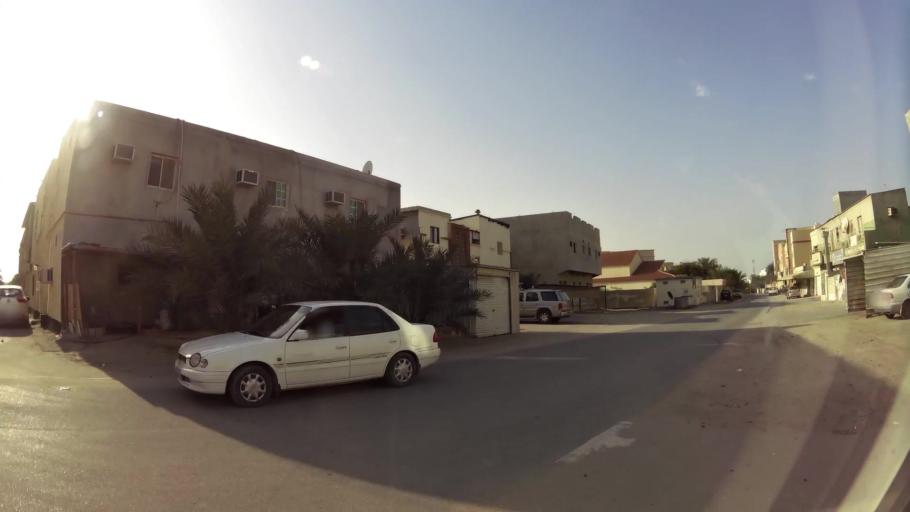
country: BH
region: Manama
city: Jidd Hafs
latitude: 26.2134
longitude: 50.5040
